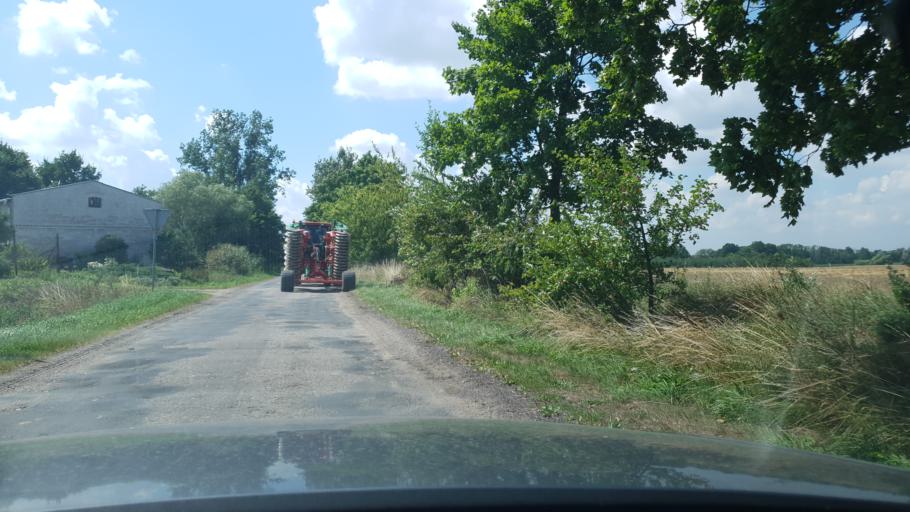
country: PL
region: Kujawsko-Pomorskie
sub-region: Powiat wabrzeski
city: Pluznica
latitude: 53.3222
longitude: 18.8307
